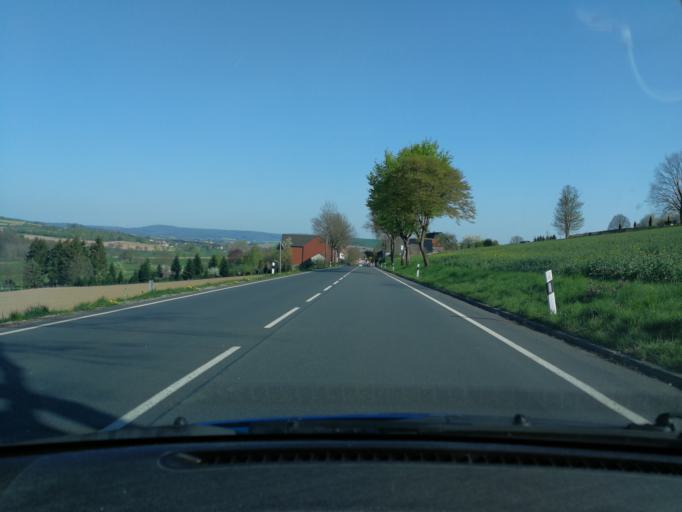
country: DE
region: Lower Saxony
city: Bodenfelde
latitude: 51.6807
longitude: 9.5722
